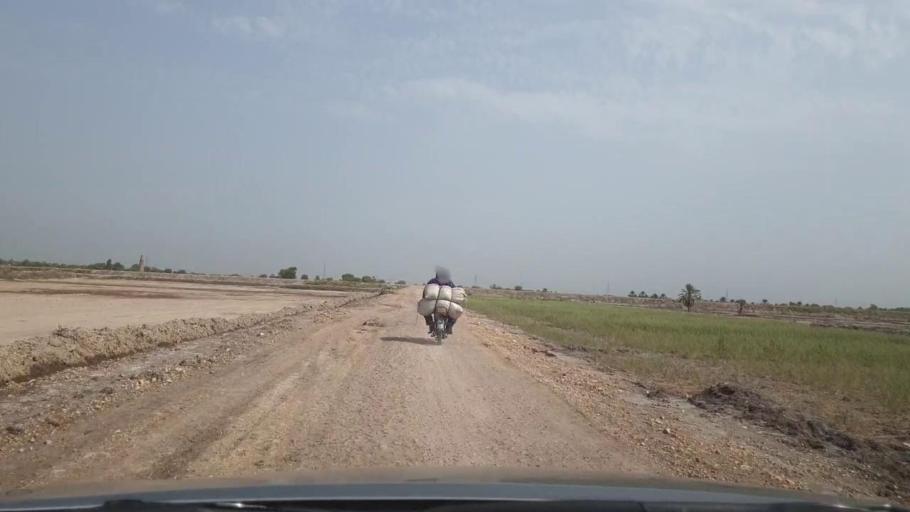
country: PK
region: Sindh
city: Rohri
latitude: 27.6769
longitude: 69.0259
